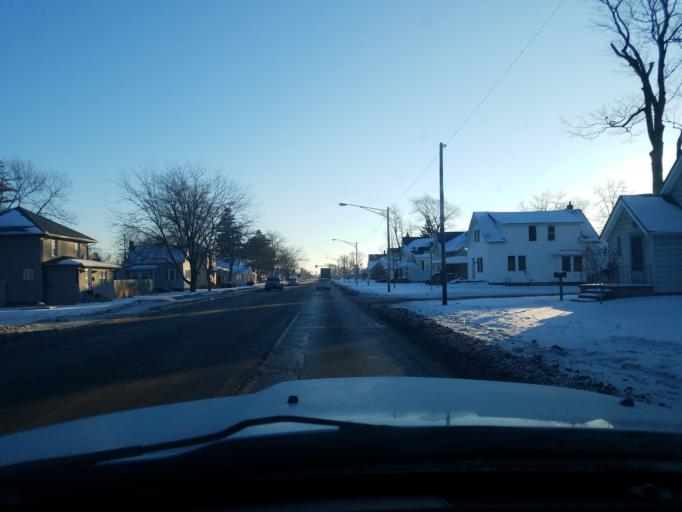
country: US
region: Indiana
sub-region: Elkhart County
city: Nappanee
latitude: 41.4427
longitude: -85.9917
